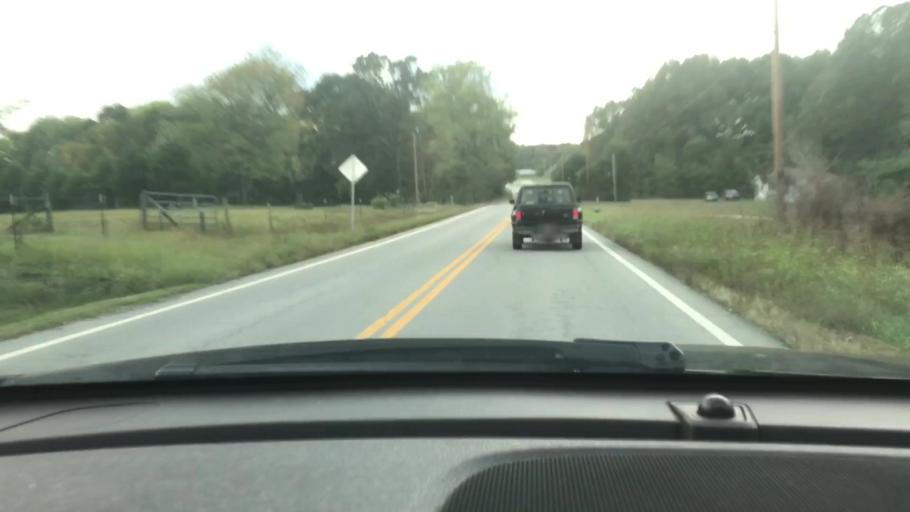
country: US
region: Tennessee
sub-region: Dickson County
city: Charlotte
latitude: 36.2120
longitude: -87.2647
